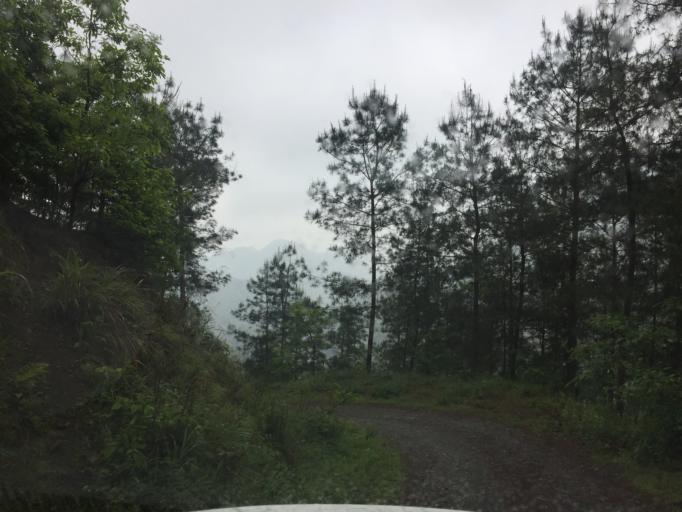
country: CN
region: Guizhou Sheng
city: Donghua
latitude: 28.0499
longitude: 108.1059
